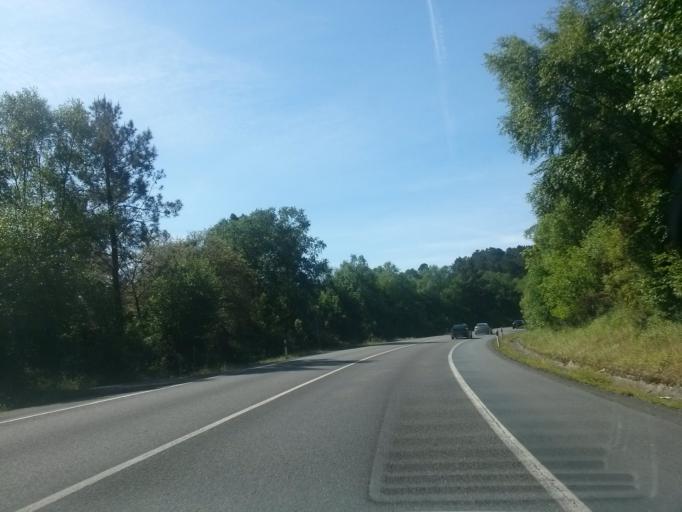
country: ES
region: Galicia
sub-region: Provincia de Lugo
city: Lugo
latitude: 43.0012
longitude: -7.5828
